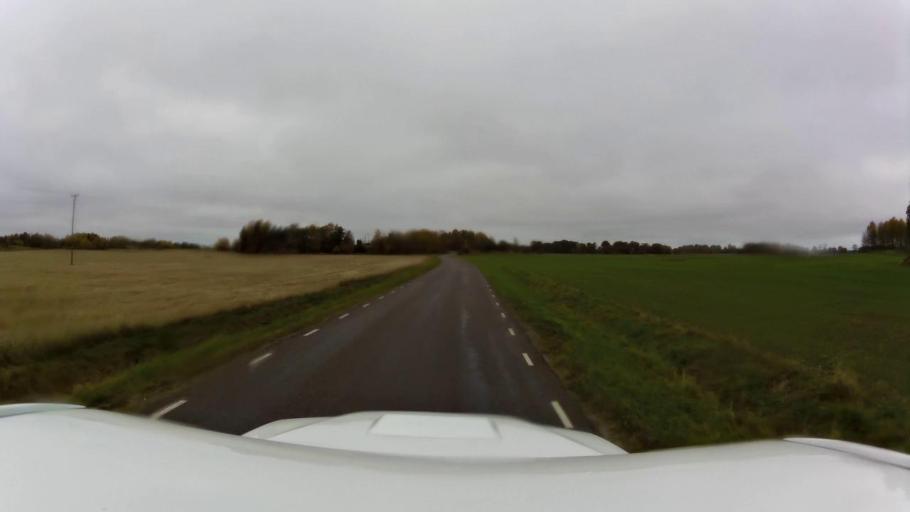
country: SE
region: OEstergoetland
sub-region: Linkopings Kommun
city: Linghem
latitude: 58.4774
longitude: 15.7271
